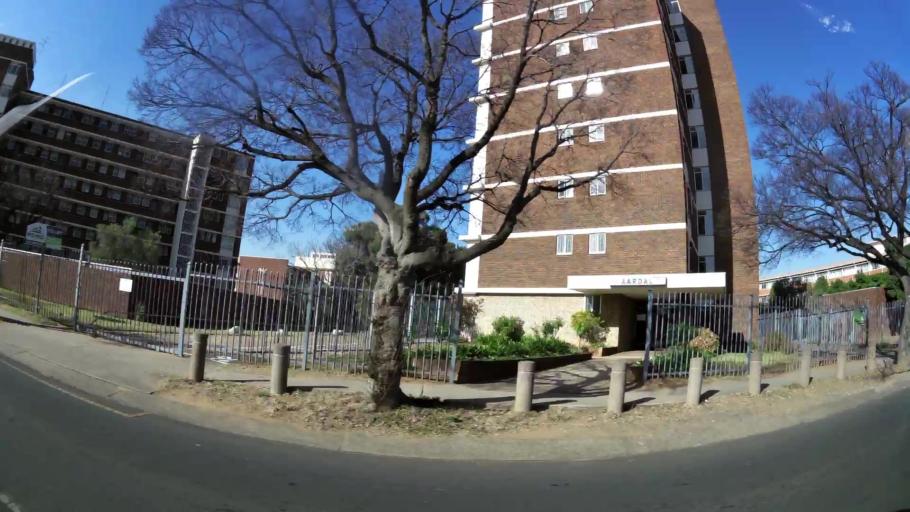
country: ZA
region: Gauteng
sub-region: City of Tshwane Metropolitan Municipality
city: Pretoria
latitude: -25.7294
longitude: 28.2457
